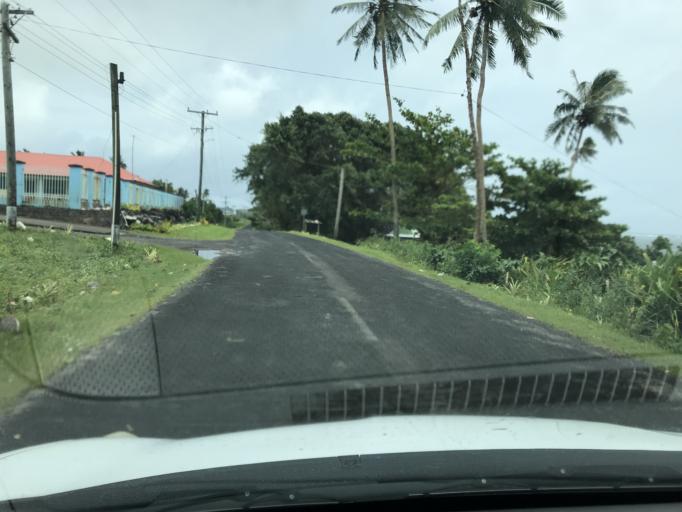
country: WS
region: Va`a-o-Fonoti
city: Samamea
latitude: -14.0448
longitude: -171.4377
